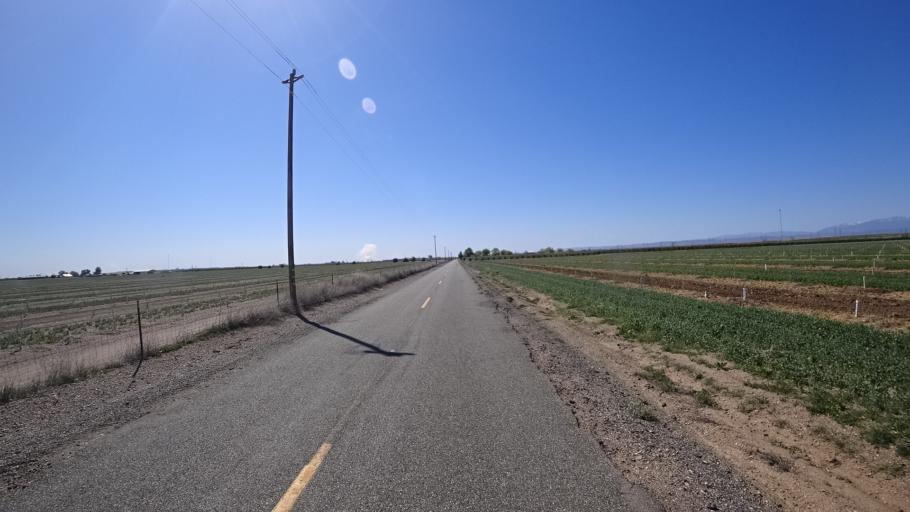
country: US
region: California
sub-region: Glenn County
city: Orland
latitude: 39.6369
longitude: -122.2534
